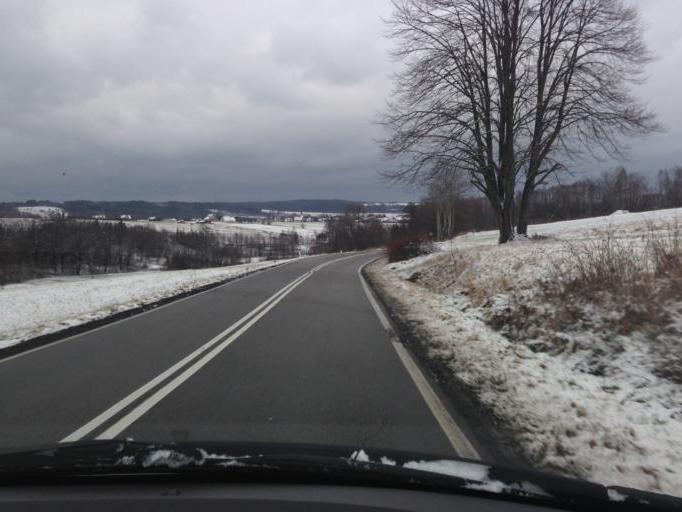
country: PL
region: Lesser Poland Voivodeship
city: Stary Wisnicz
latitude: 49.8515
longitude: 20.5117
